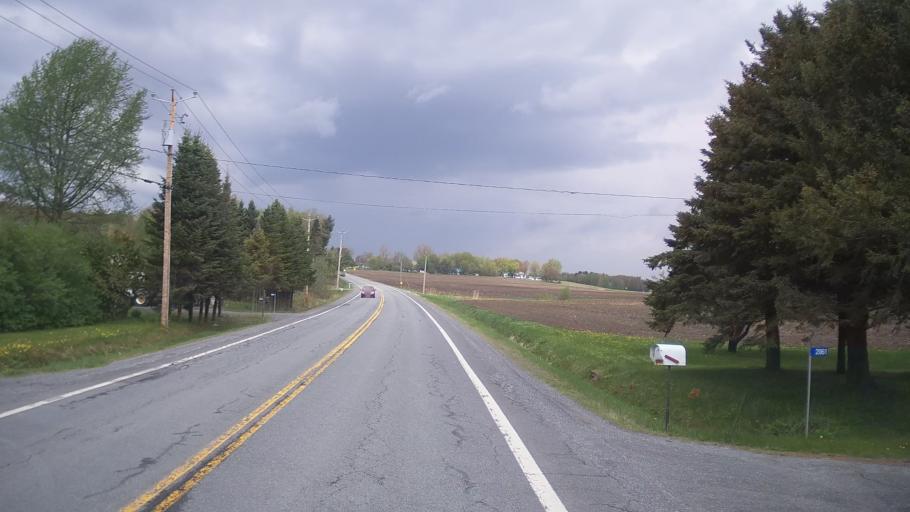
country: CA
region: Quebec
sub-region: Monteregie
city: Farnham
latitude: 45.2415
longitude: -72.8837
